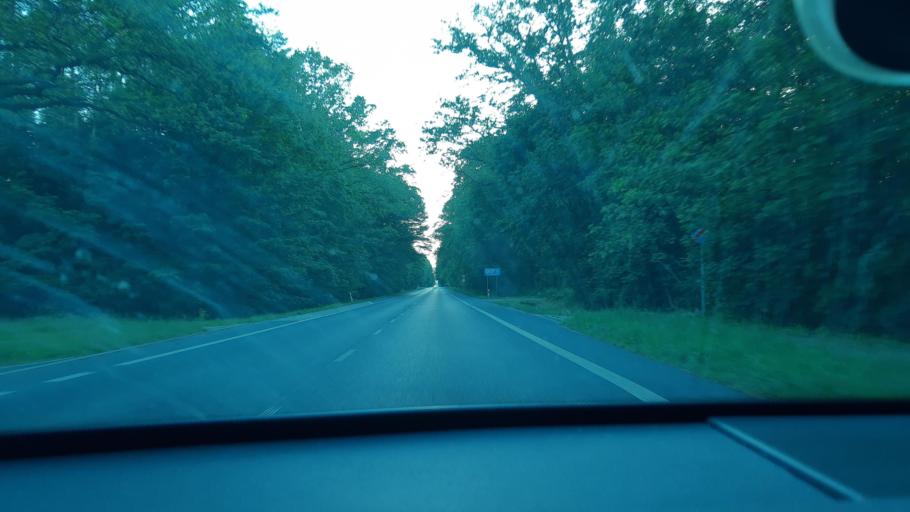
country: PL
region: Lodz Voivodeship
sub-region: Powiat zdunskowolski
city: Zapolice
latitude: 51.6042
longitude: 18.8340
